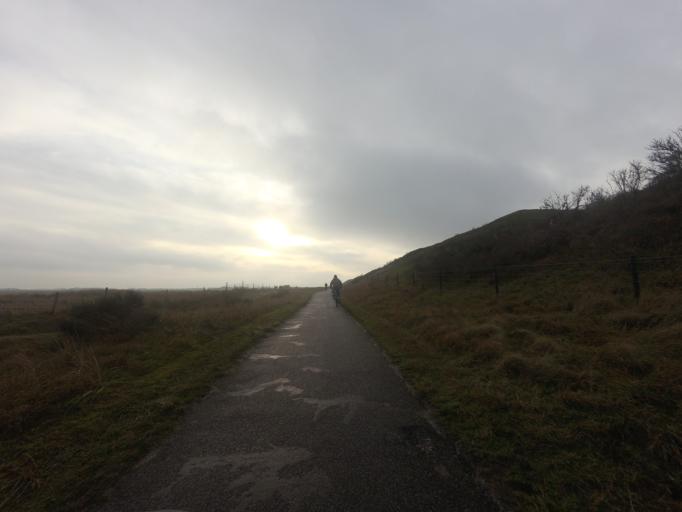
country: NL
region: North Holland
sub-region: Gemeente Texel
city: Den Burg
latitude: 53.1423
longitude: 4.8301
